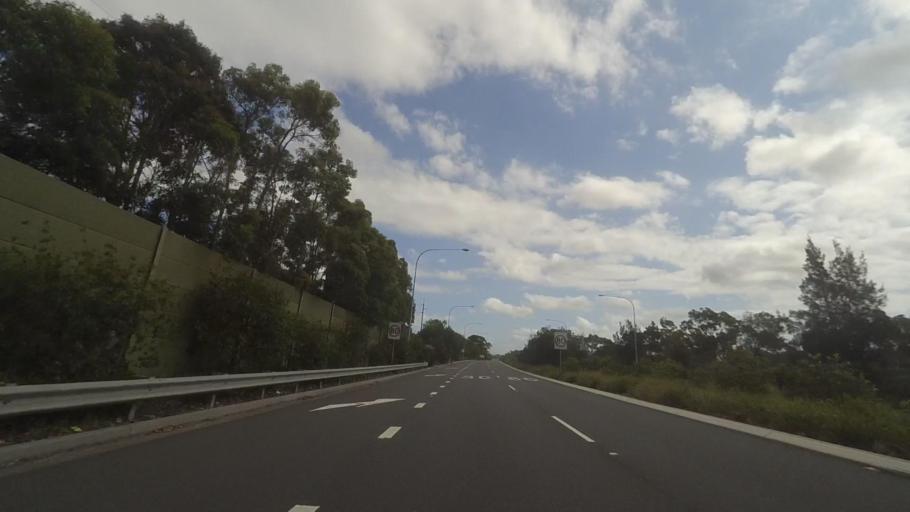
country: AU
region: New South Wales
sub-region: Sutherland Shire
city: Menai
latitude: -34.0247
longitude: 151.0076
